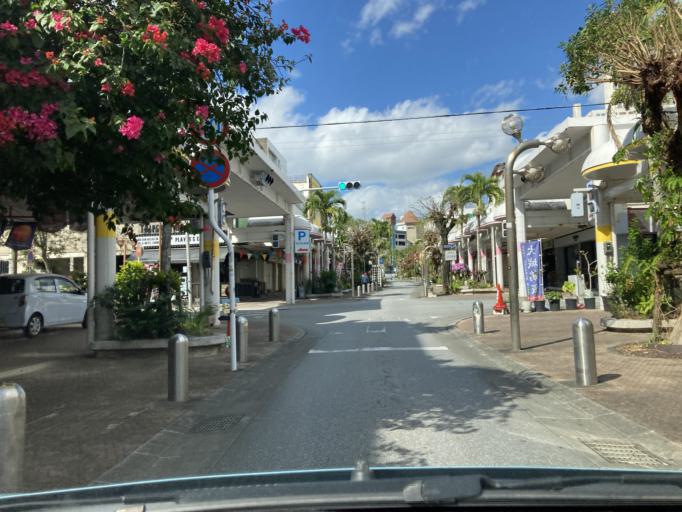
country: JP
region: Okinawa
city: Okinawa
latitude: 26.3387
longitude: 127.8006
